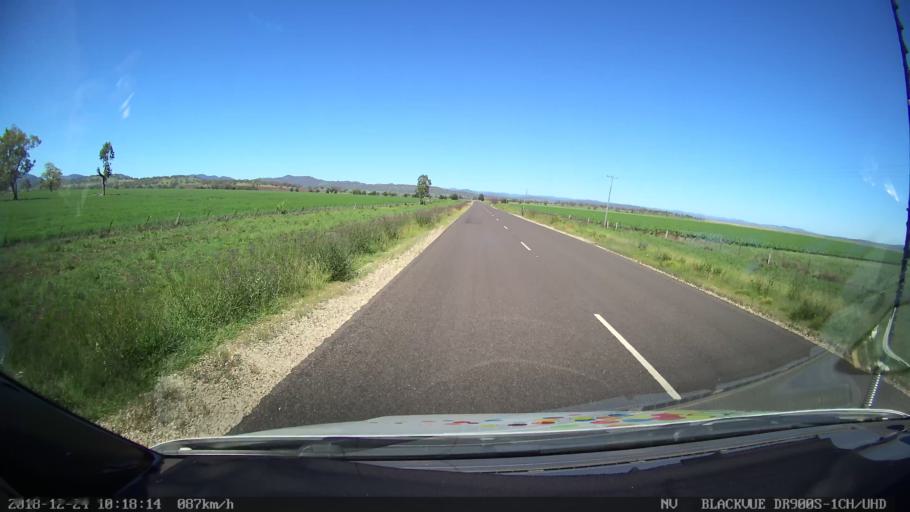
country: AU
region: New South Wales
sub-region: Liverpool Plains
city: Quirindi
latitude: -31.7230
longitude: 150.5794
